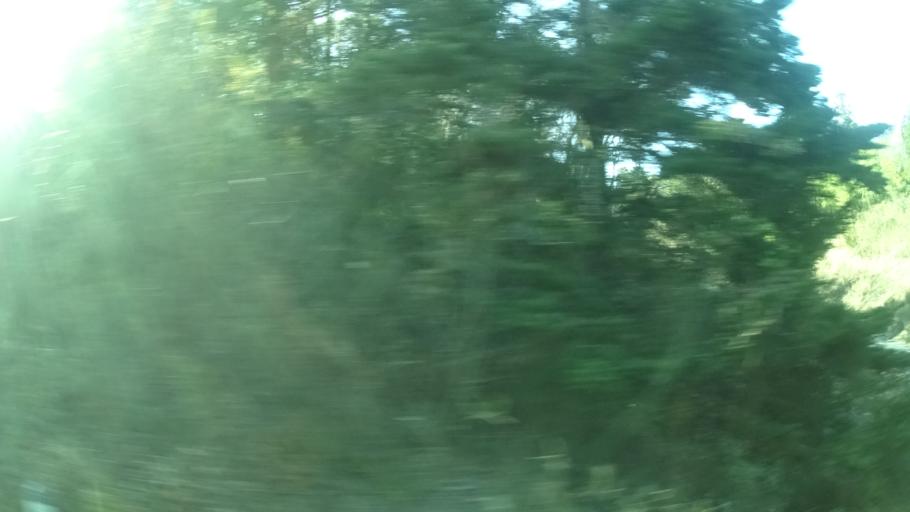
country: JP
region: Fukushima
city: Namie
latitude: 37.7269
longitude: 140.9518
